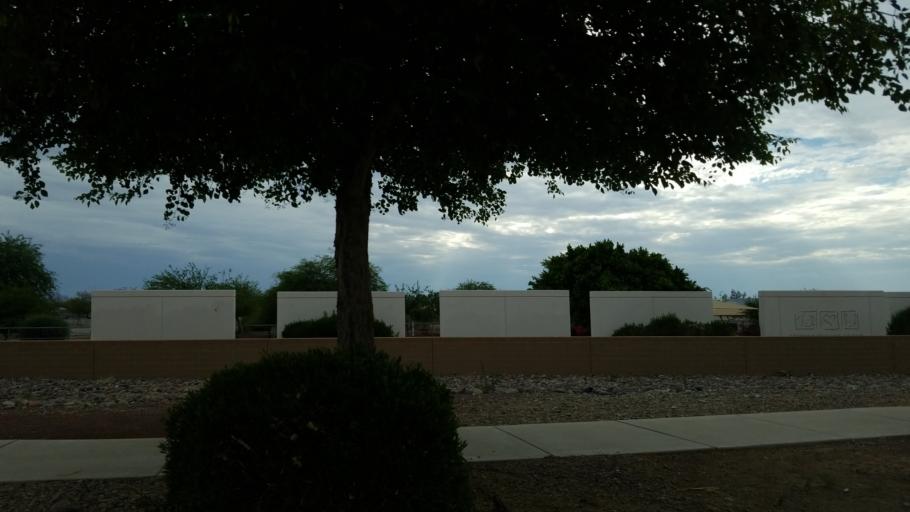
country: US
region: Arizona
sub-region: Maricopa County
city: Laveen
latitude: 33.3617
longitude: -112.0920
